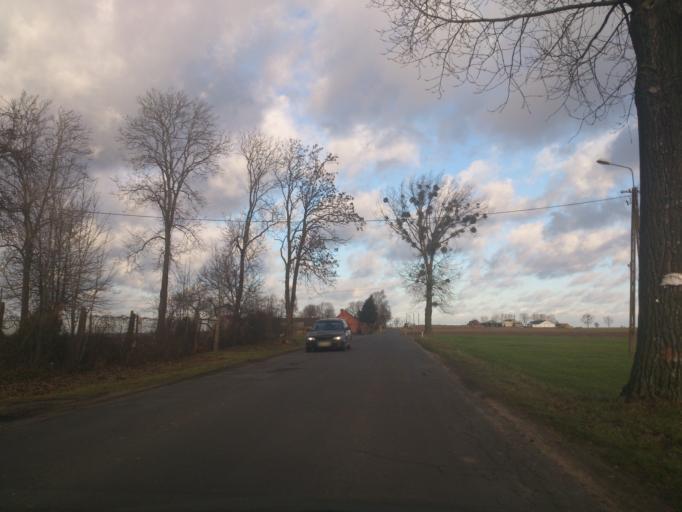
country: PL
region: Kujawsko-Pomorskie
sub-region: Powiat torunski
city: Obrowo
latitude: 53.0225
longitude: 18.8643
